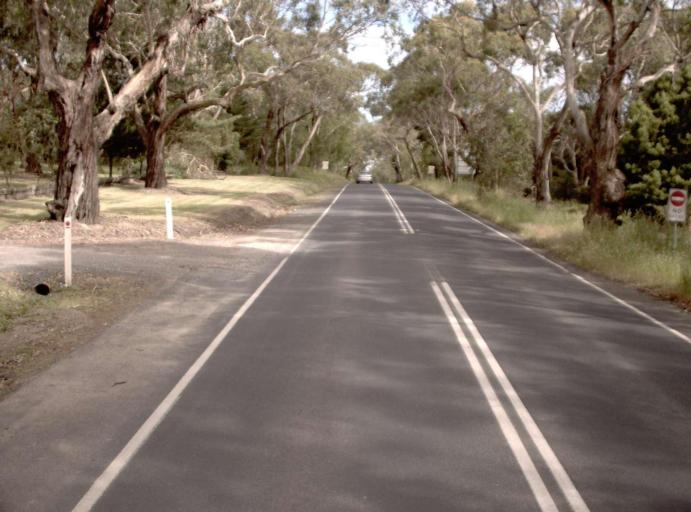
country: AU
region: Victoria
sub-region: Bass Coast
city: Phillip Island
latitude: -38.4862
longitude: 145.2617
